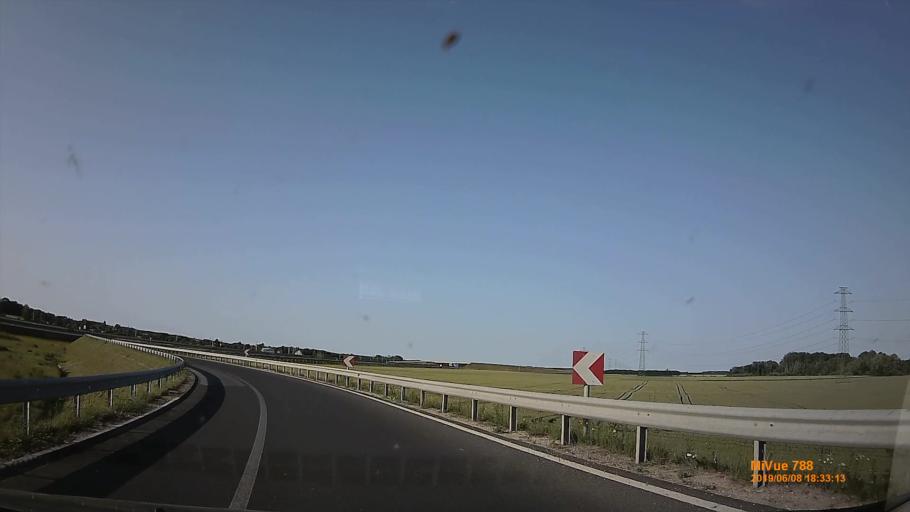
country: HU
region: Vas
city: Sarvar
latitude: 47.3572
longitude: 16.9065
